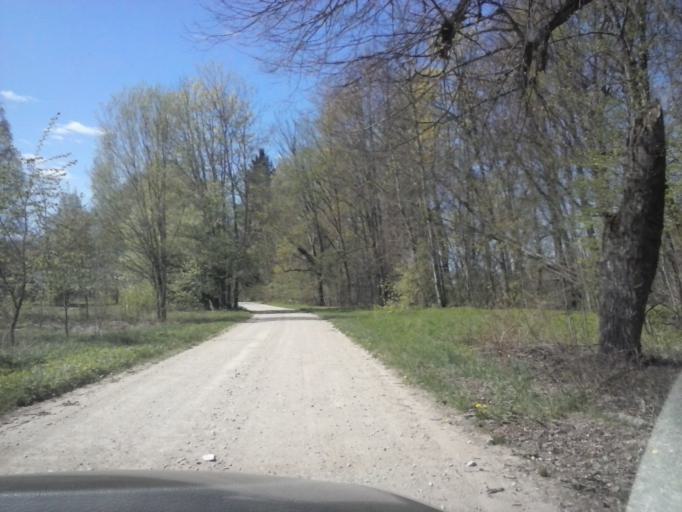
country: EE
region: Valgamaa
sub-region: Torva linn
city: Torva
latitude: 58.2339
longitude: 25.8964
